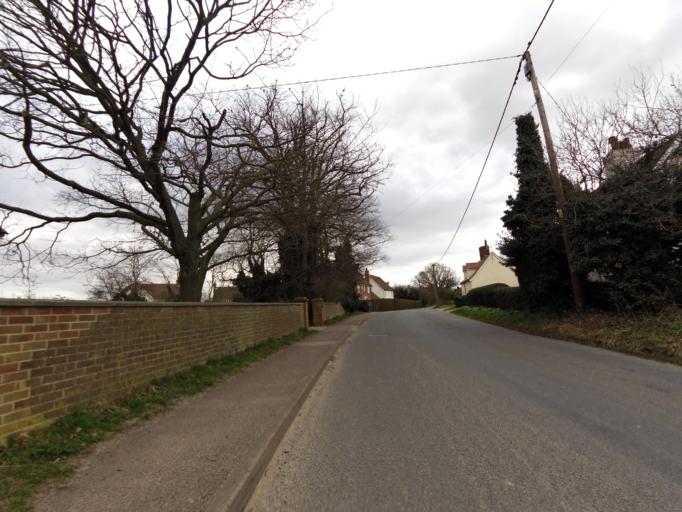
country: GB
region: England
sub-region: Suffolk
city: Felixstowe
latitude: 52.0126
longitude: 1.3153
